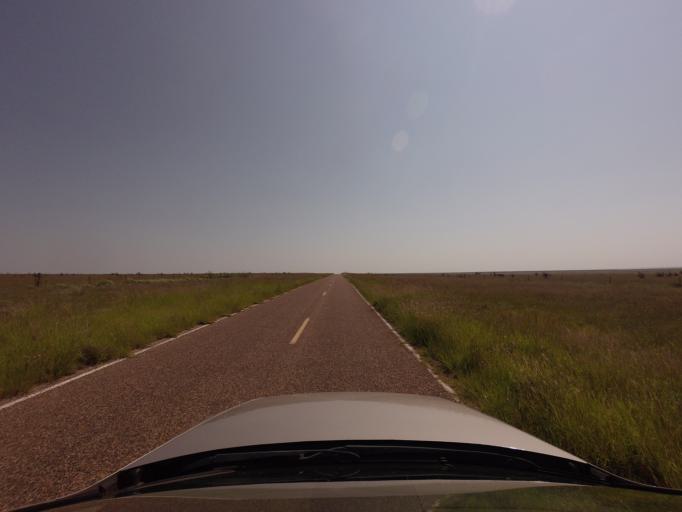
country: US
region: New Mexico
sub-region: Curry County
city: Cannon Air Force Base
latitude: 34.6331
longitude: -103.4133
